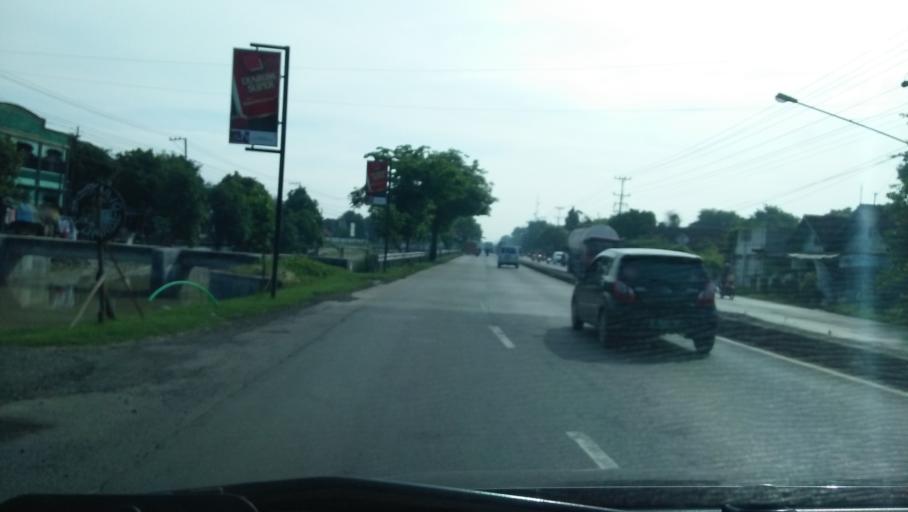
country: ID
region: Central Java
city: Demak
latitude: -6.9273
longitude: 110.5532
